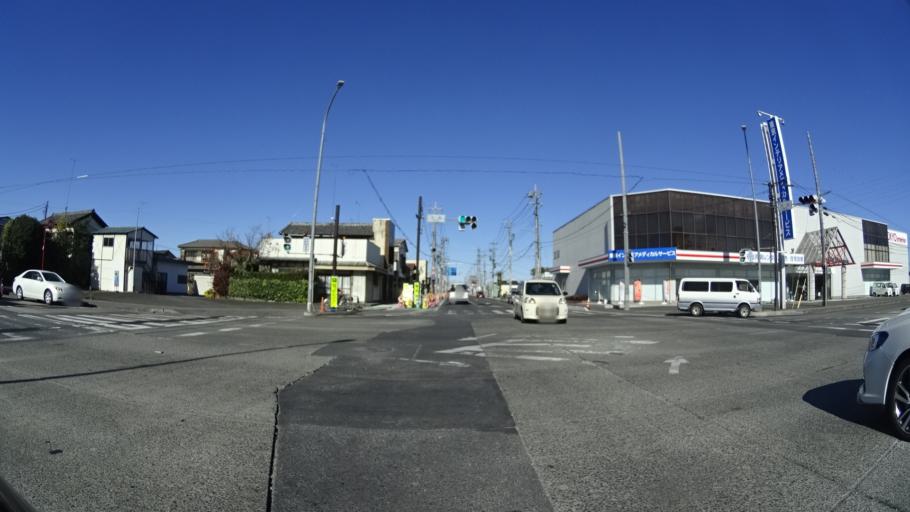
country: JP
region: Tochigi
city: Tochigi
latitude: 36.3943
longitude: 139.7370
